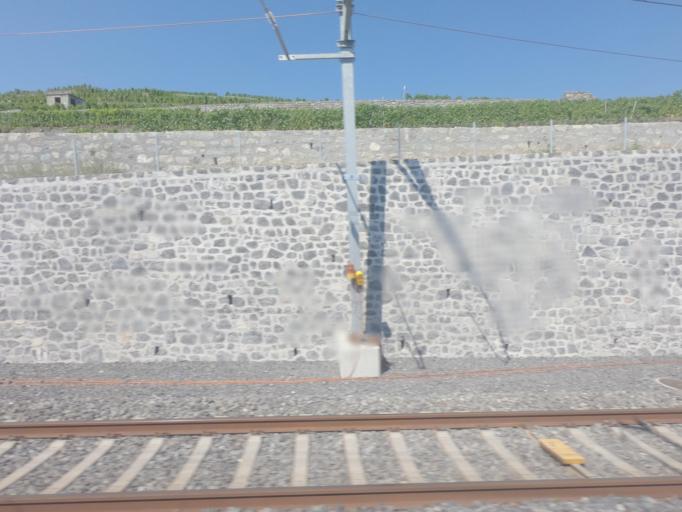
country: CH
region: Vaud
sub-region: Lavaux-Oron District
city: Cully
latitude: 46.4881
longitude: 6.7204
